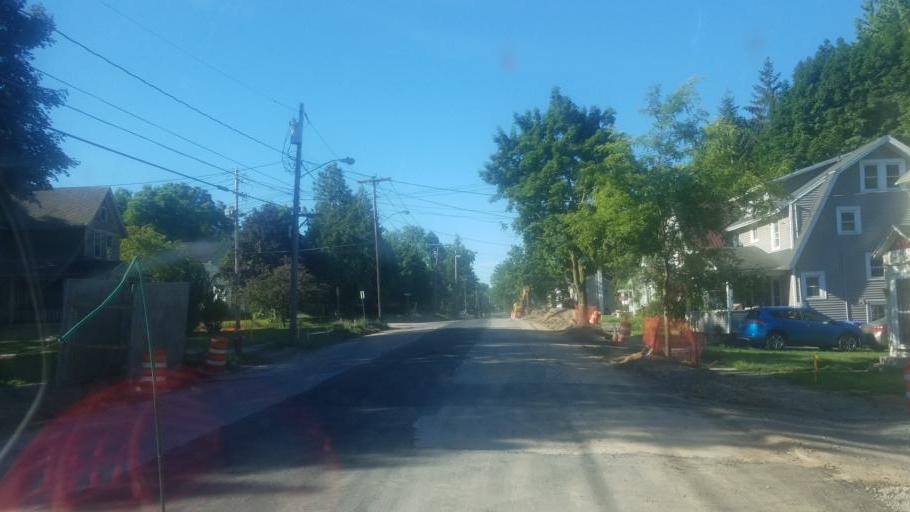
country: US
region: New York
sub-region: Wayne County
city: Newark
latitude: 43.0385
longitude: -77.0962
